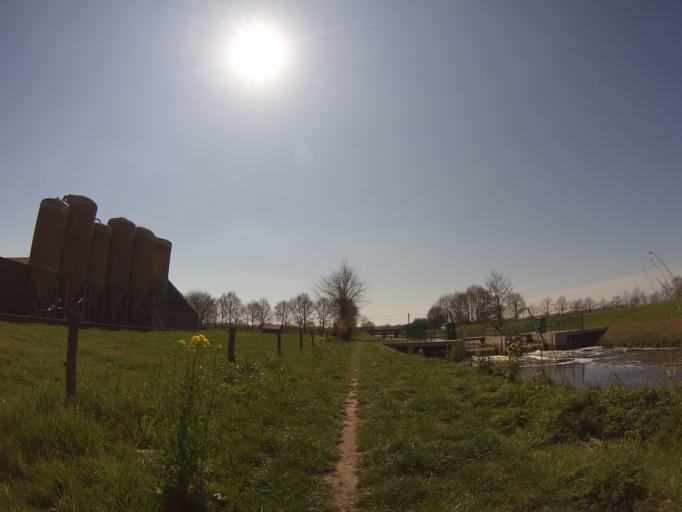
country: NL
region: Utrecht
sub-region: Gemeente Utrechtse Heuvelrug
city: Overberg
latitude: 52.0528
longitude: 5.4845
